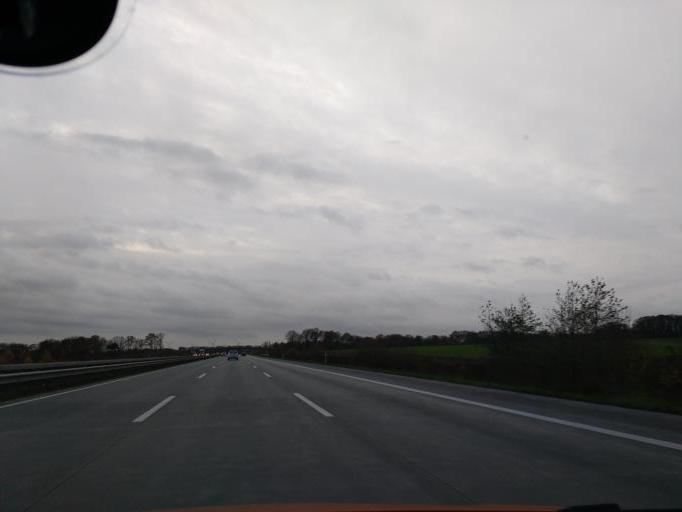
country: DE
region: Lower Saxony
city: Gross Meckelsen
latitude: 53.2462
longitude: 9.4102
